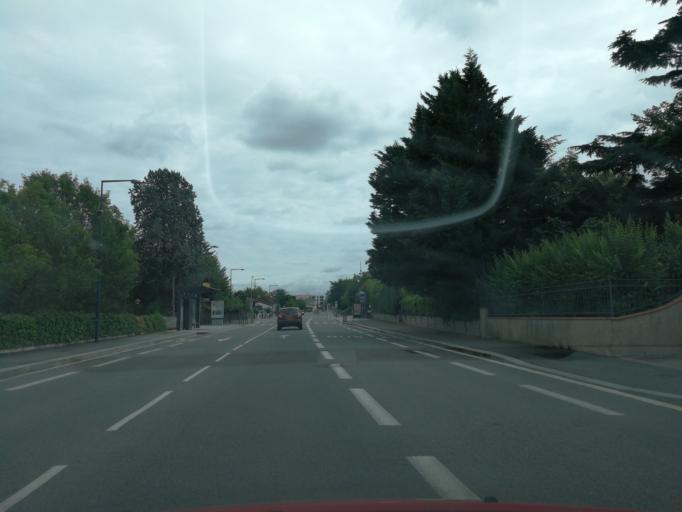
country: FR
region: Midi-Pyrenees
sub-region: Departement de la Haute-Garonne
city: Ramonville-Saint-Agne
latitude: 43.5440
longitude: 1.4769
